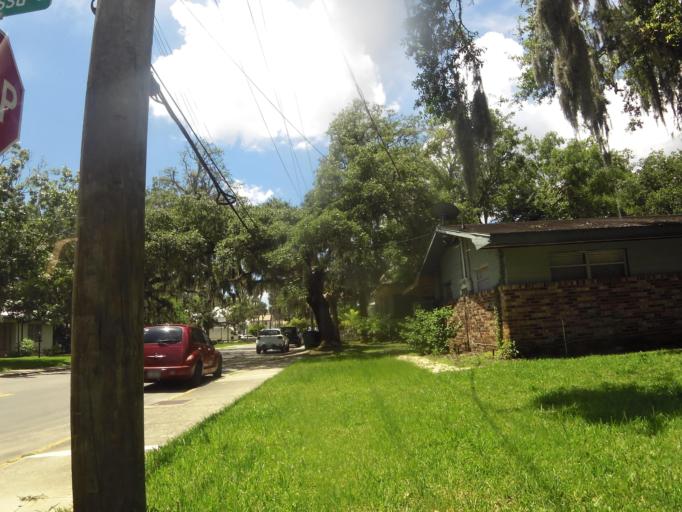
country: US
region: Florida
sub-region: Saint Johns County
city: Saint Augustine
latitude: 29.8956
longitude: -81.3192
